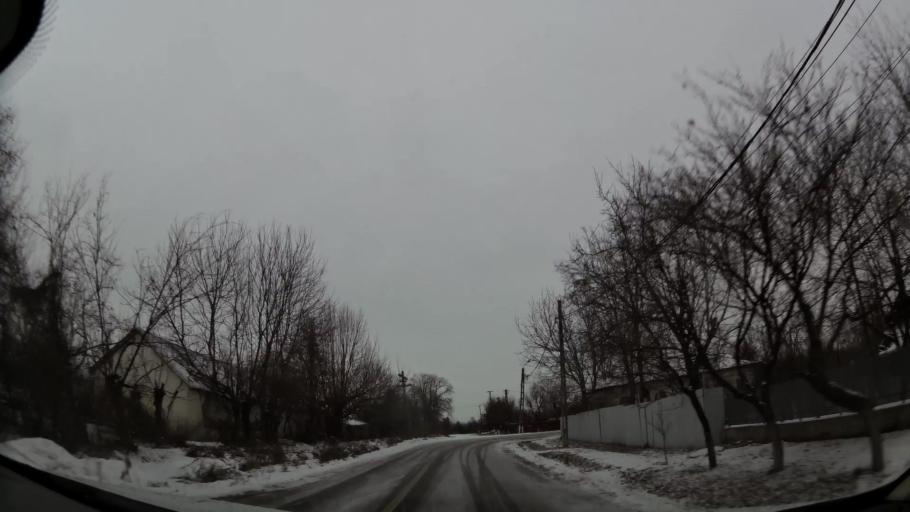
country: RO
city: Fantanele
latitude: 44.7323
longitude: 25.8922
